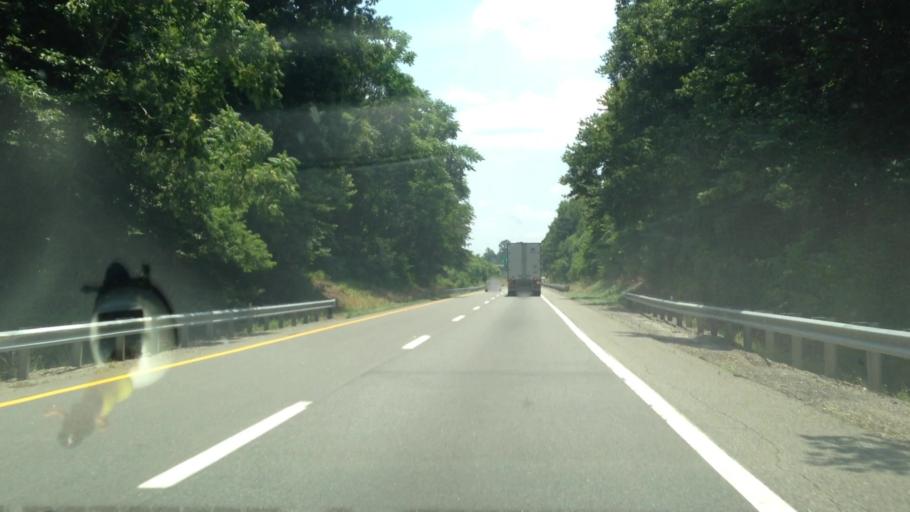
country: US
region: Virginia
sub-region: City of Martinsville
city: Martinsville
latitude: 36.6315
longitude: -79.8845
